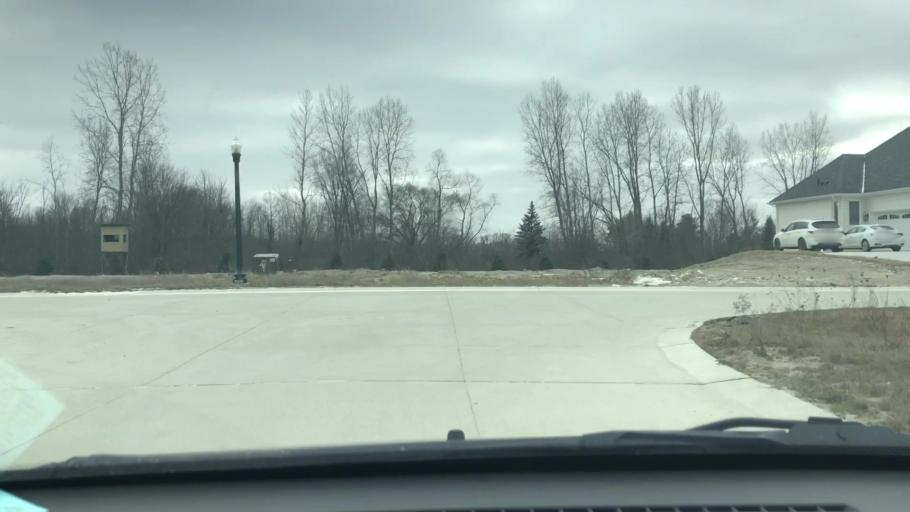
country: US
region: Michigan
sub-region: Macomb County
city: Romeo
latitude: 42.7407
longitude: -83.0131
